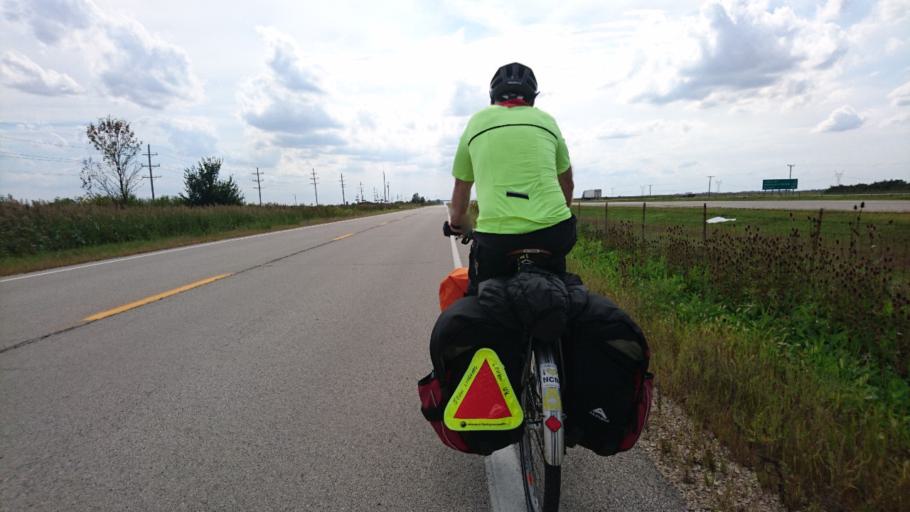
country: US
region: Illinois
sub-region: Grundy County
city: Gardner
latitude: 41.1653
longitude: -88.3371
